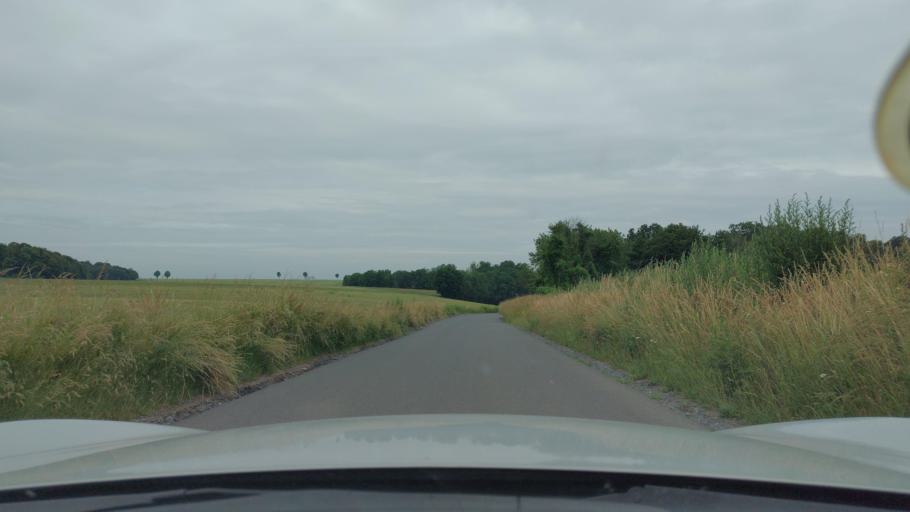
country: FR
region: Picardie
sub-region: Departement de l'Oise
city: Betz
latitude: 49.1415
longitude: 2.9680
